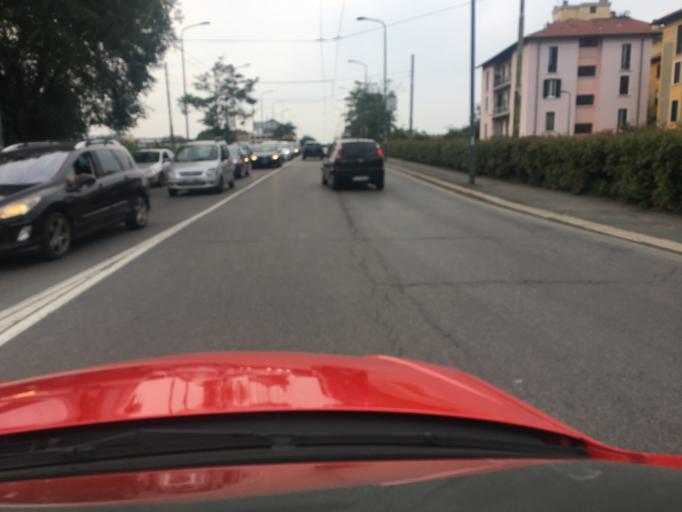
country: IT
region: Lombardy
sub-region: Citta metropolitana di Milano
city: Chiaravalle
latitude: 45.4449
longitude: 9.2242
